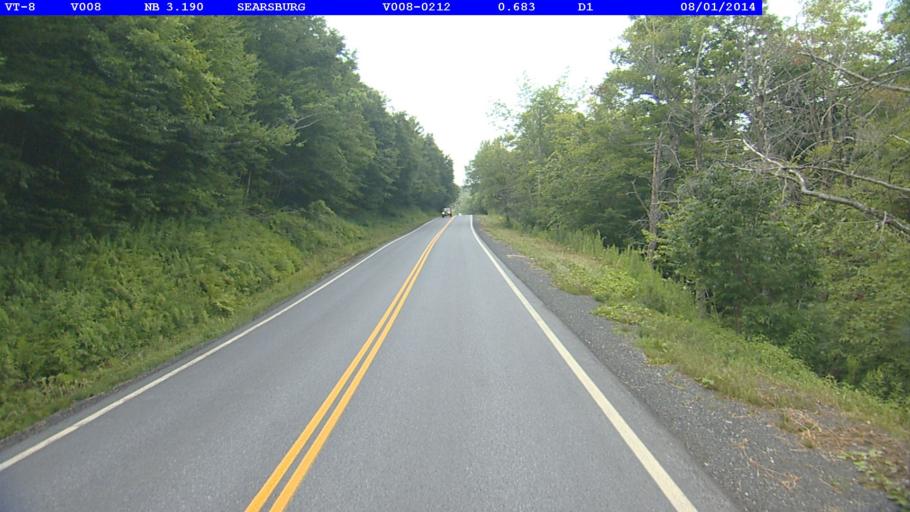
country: US
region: Vermont
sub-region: Windham County
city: Dover
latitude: 42.8670
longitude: -72.9707
